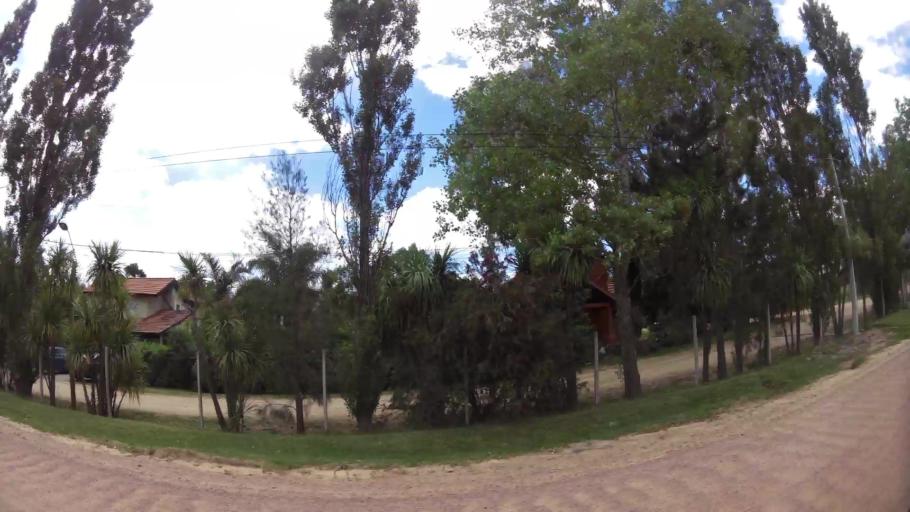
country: UY
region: Canelones
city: Colonia Nicolich
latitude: -34.8200
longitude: -55.9905
